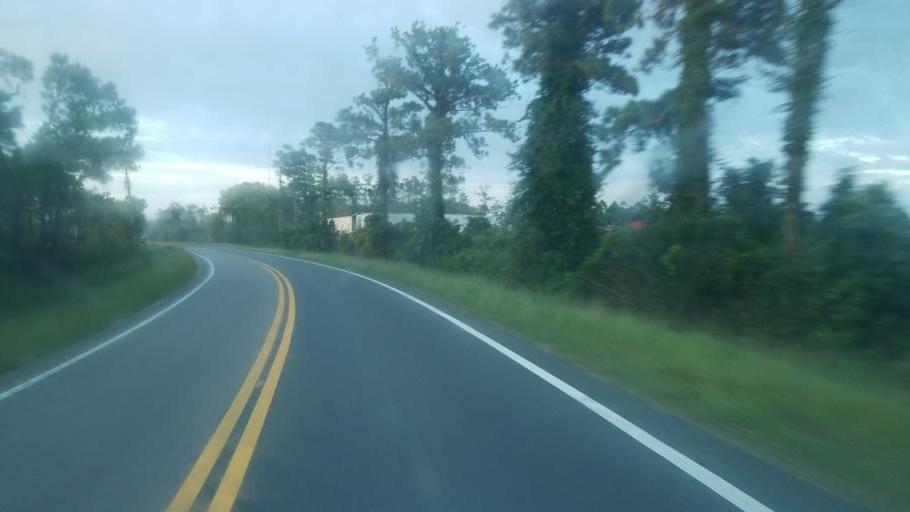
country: US
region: North Carolina
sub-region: Dare County
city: Wanchese
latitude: 35.8720
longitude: -75.6539
